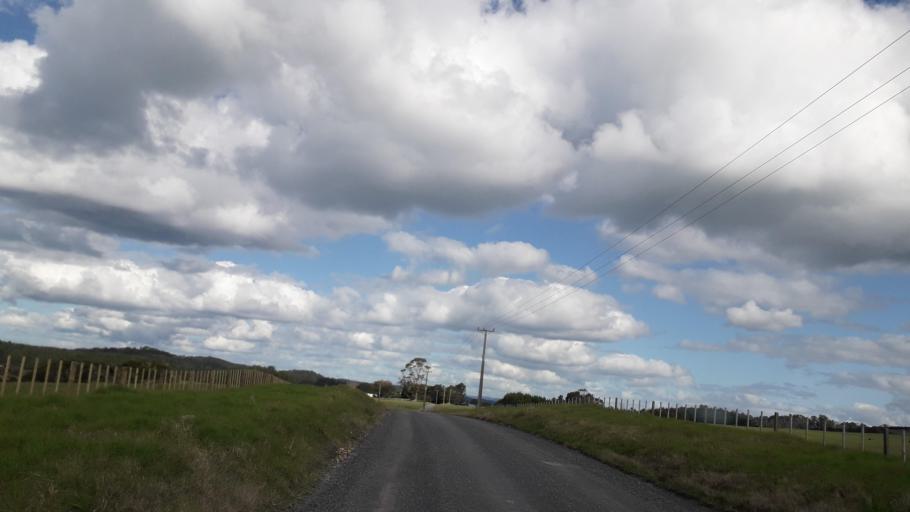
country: NZ
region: Northland
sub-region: Far North District
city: Kerikeri
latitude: -35.1477
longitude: 174.0381
